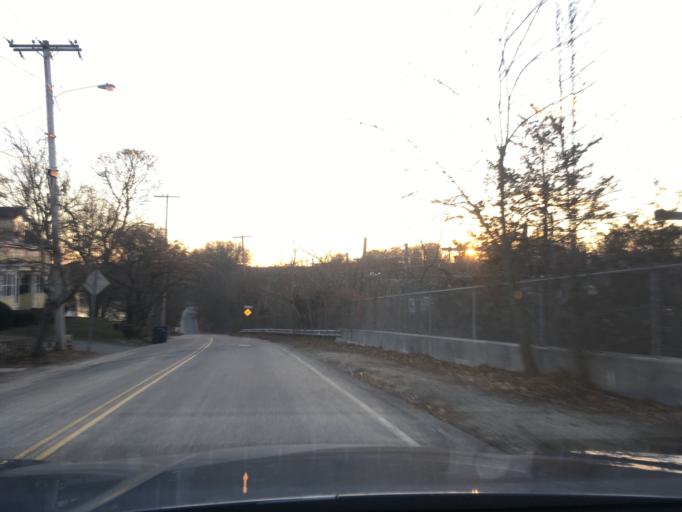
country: US
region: Rhode Island
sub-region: Kent County
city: East Greenwich
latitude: 41.6549
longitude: -71.4511
